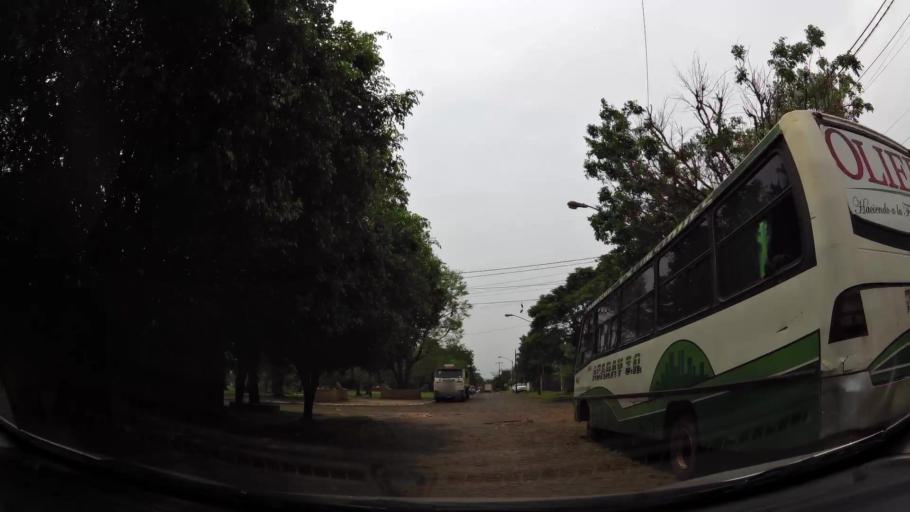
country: PY
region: Alto Parana
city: Presidente Franco
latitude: -25.5541
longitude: -54.6265
